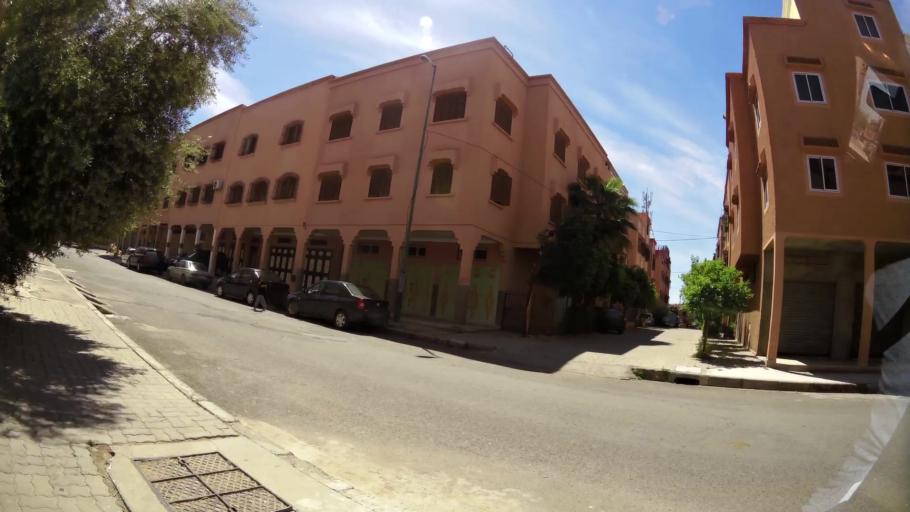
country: MA
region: Marrakech-Tensift-Al Haouz
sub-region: Marrakech
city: Marrakesh
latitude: 31.6414
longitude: -8.0631
